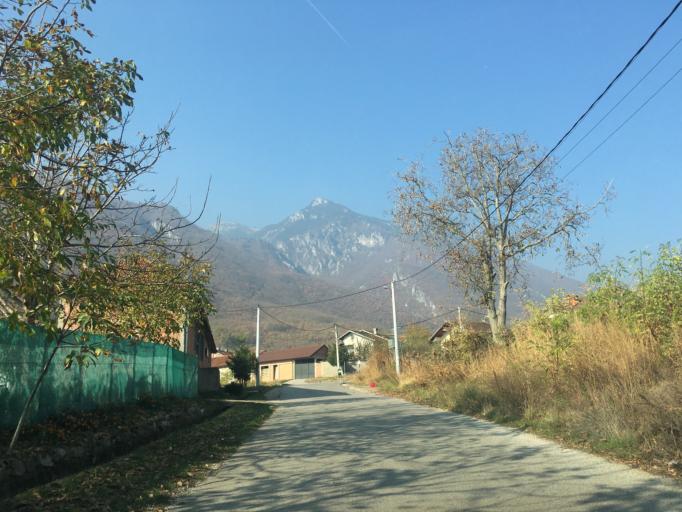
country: XK
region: Gjakova
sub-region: Komuna e Decanit
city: Strellc i Eperm
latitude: 42.5961
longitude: 20.2938
